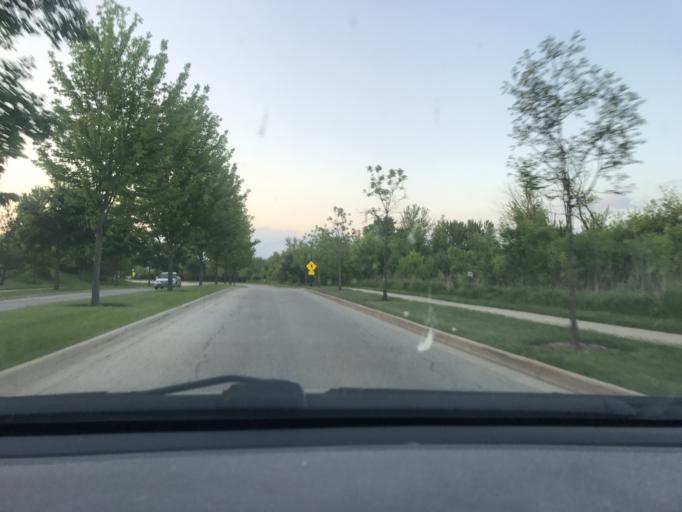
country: US
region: Illinois
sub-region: Kane County
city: South Elgin
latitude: 42.0154
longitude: -88.3562
